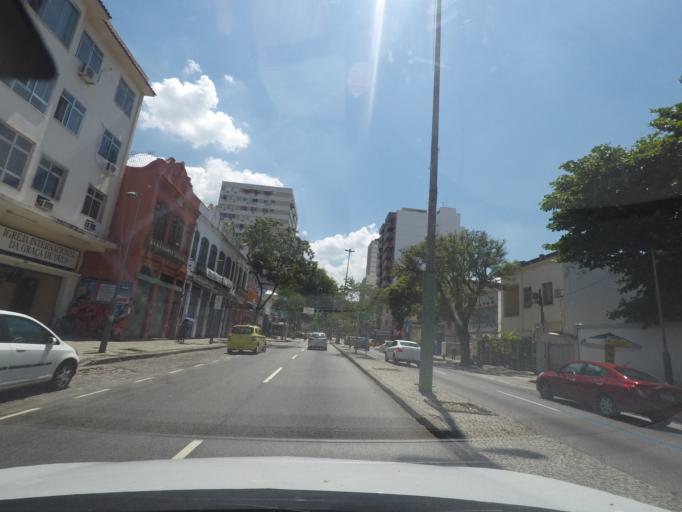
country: BR
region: Rio de Janeiro
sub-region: Rio De Janeiro
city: Rio de Janeiro
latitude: -22.9149
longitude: -43.2414
